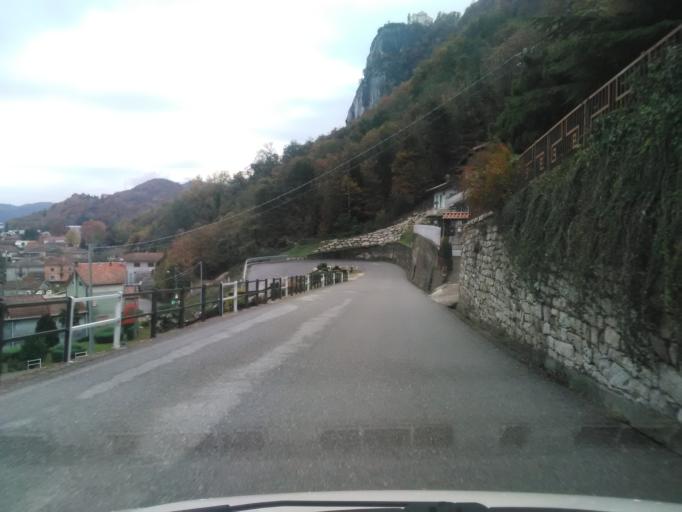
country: IT
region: Piedmont
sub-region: Provincia Verbano-Cusio-Ossola
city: Madonna del Sasso
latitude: 45.7940
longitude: 8.3769
